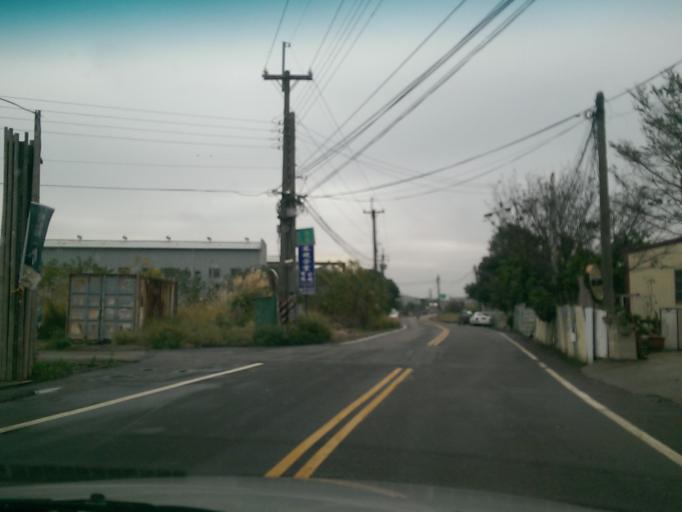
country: TW
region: Taiwan
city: Fengyuan
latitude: 24.2420
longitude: 120.6149
